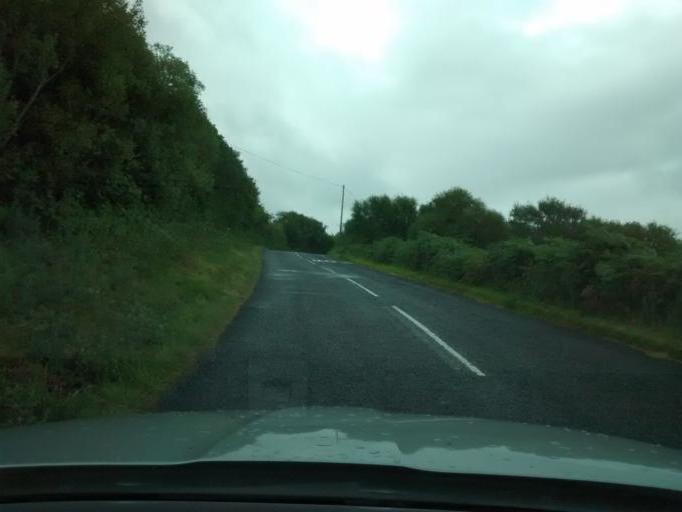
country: GB
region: Scotland
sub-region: North Ayrshire
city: Isle of Arran
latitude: 55.6181
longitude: -5.3943
